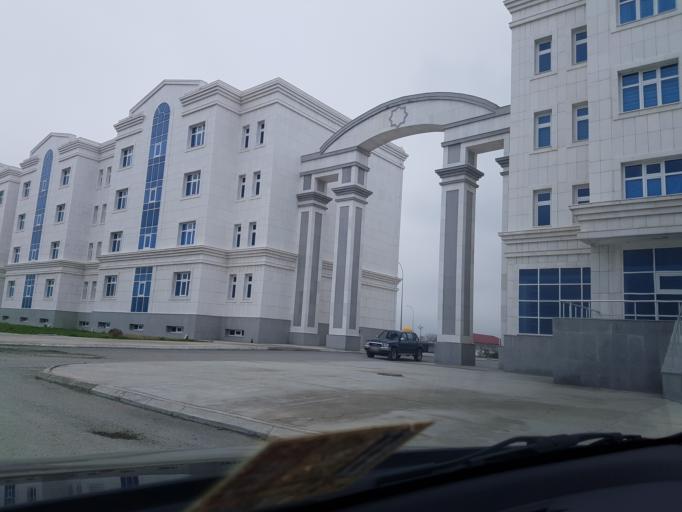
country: TM
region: Ahal
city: Abadan
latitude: 38.1642
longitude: 57.9363
